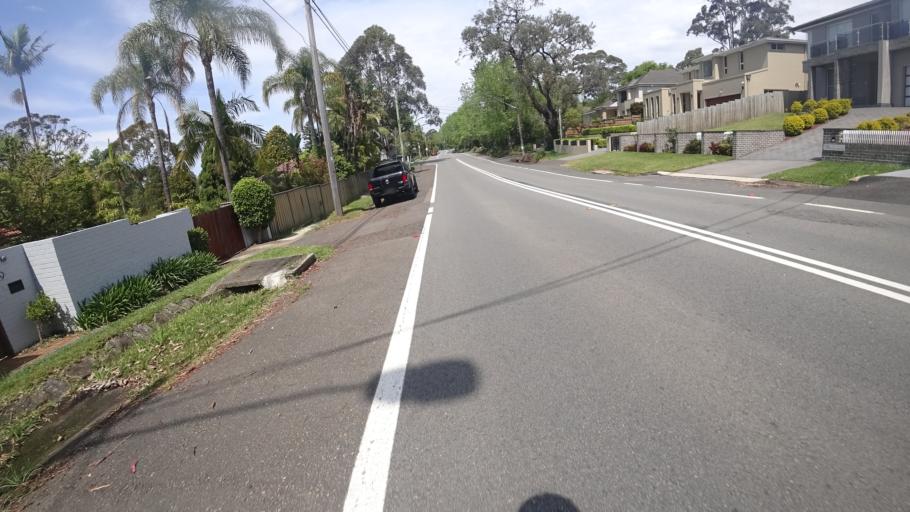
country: AU
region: New South Wales
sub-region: City of Sydney
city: North Turramurra
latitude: -33.7262
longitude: 151.1392
